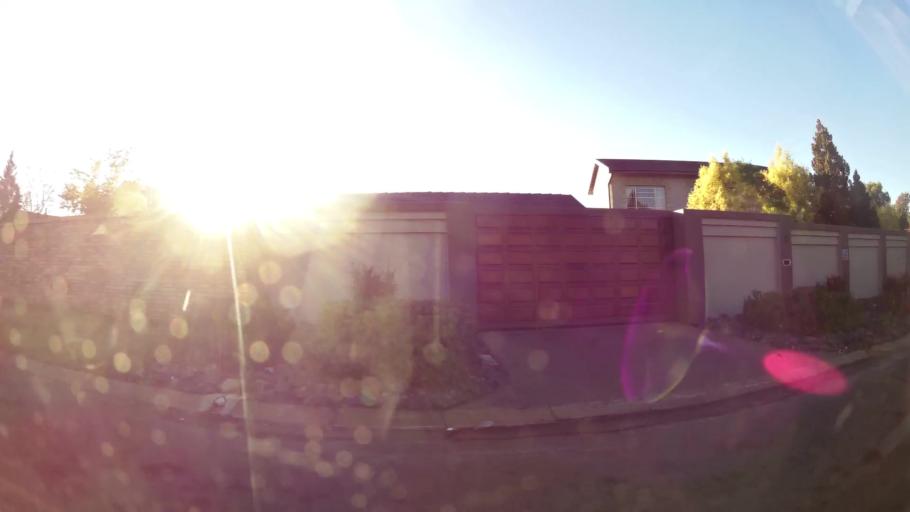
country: ZA
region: Northern Cape
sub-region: Frances Baard District Municipality
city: Kimberley
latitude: -28.7578
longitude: 24.7559
